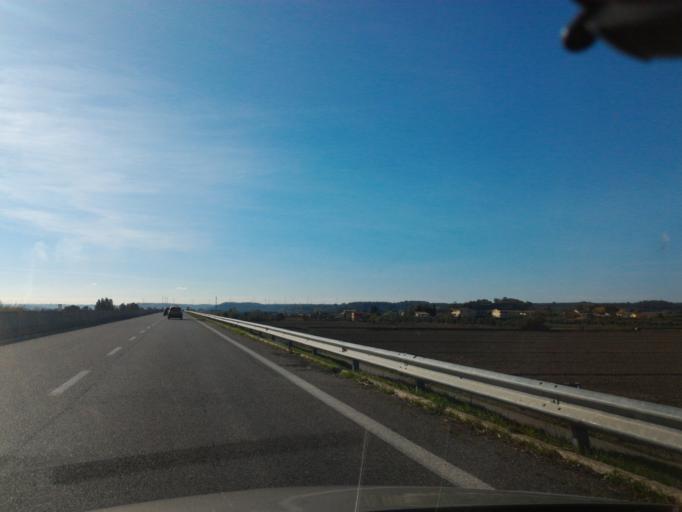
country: IT
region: Calabria
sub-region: Provincia di Crotone
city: Crotone
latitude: 39.1485
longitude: 17.0964
